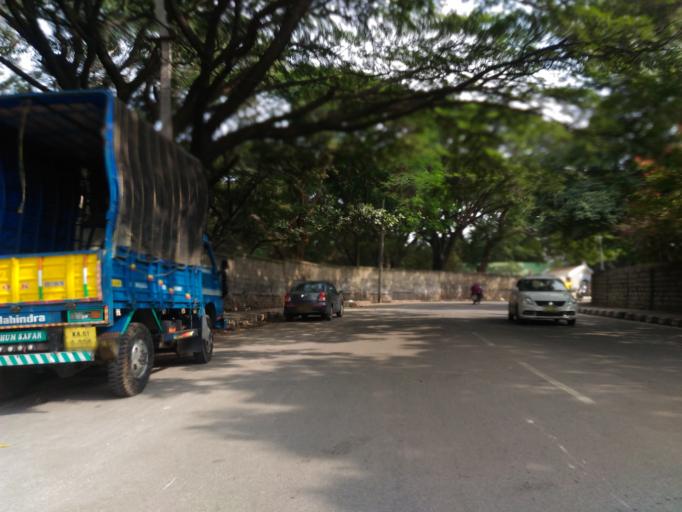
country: IN
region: Karnataka
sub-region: Bangalore Urban
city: Bangalore
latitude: 12.9519
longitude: 77.6040
